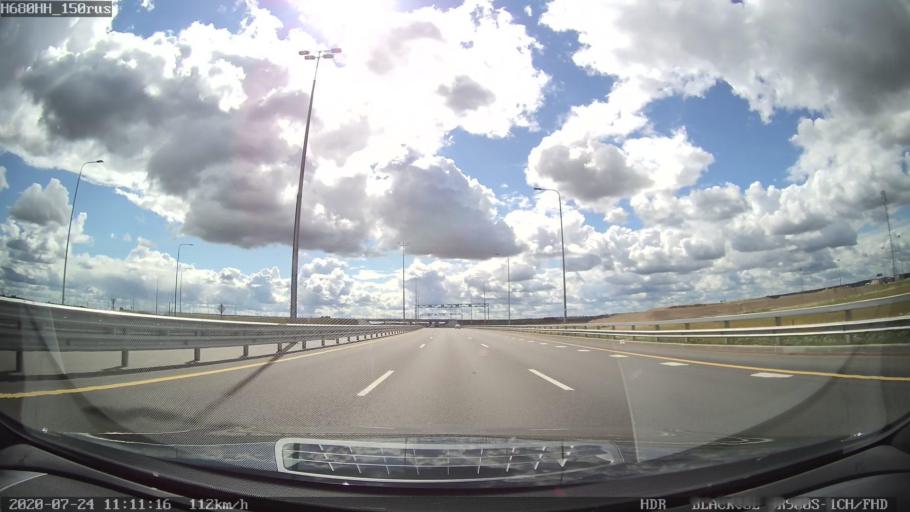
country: RU
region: St.-Petersburg
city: Tyarlevo
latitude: 59.7252
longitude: 30.5133
